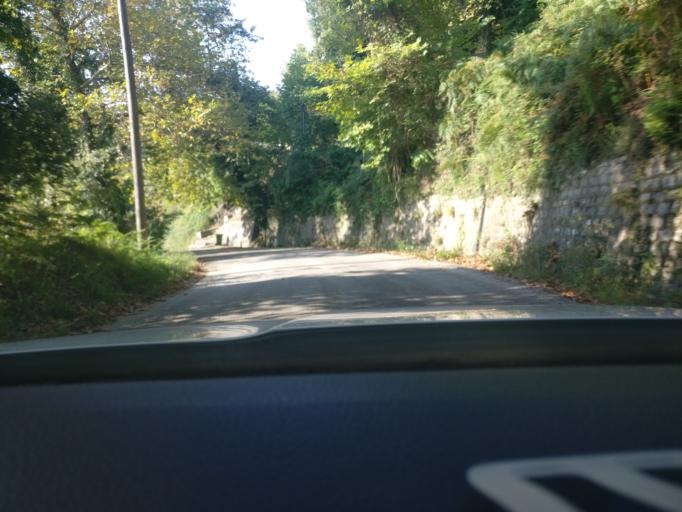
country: GR
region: Thessaly
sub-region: Nomos Magnisias
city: Zagora
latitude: 39.3808
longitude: 23.1846
